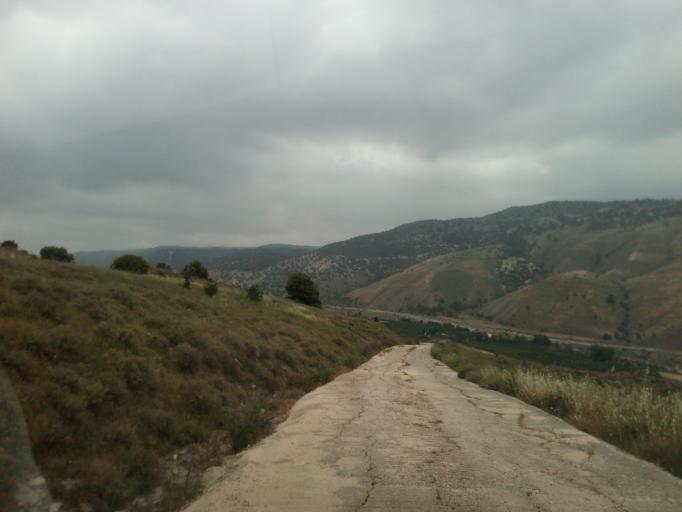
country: CY
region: Limassol
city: Pissouri
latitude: 34.8142
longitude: 32.6326
